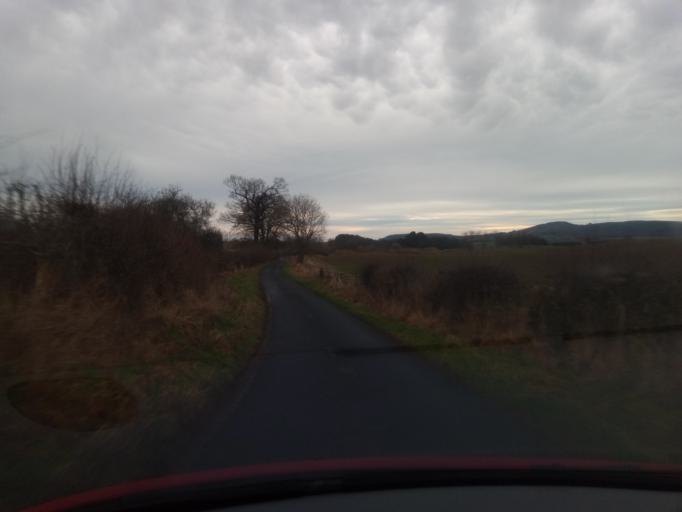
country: GB
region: England
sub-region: Northumberland
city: Wooler
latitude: 55.4927
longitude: -1.9421
